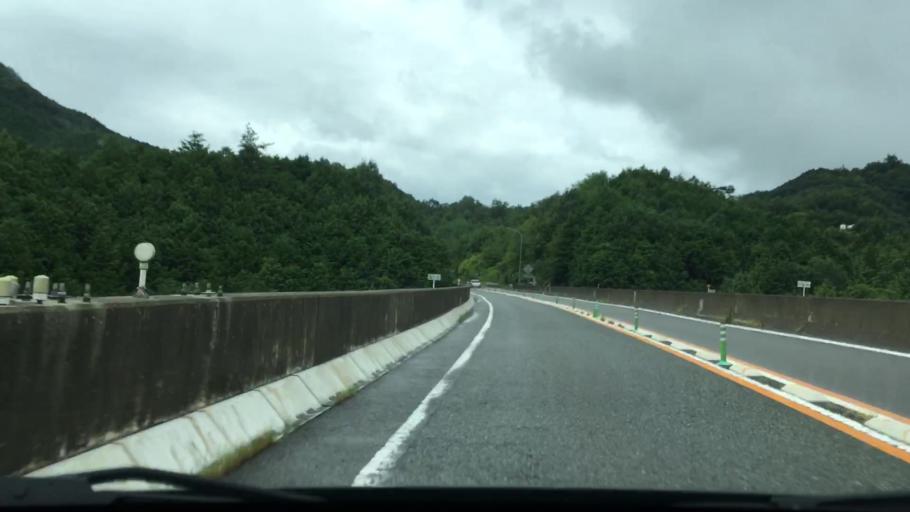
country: JP
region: Hyogo
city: Toyooka
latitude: 35.3085
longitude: 134.8259
